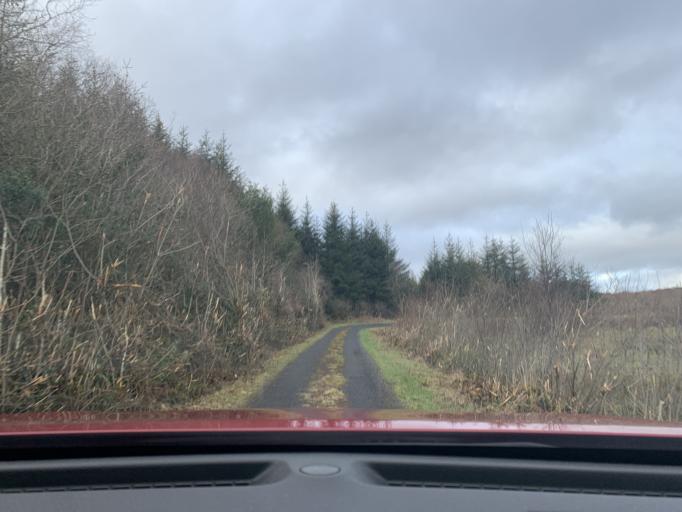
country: IE
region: Connaught
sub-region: Roscommon
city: Ballaghaderreen
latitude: 53.9277
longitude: -8.5600
